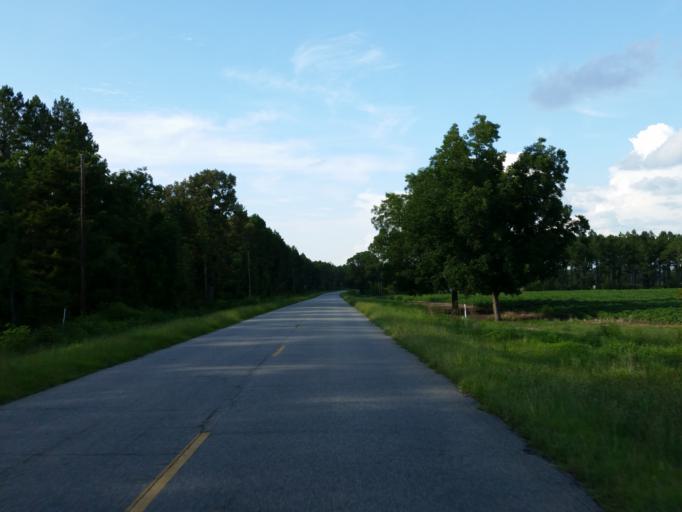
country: US
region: Georgia
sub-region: Dooly County
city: Vienna
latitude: 32.0567
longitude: -83.8272
